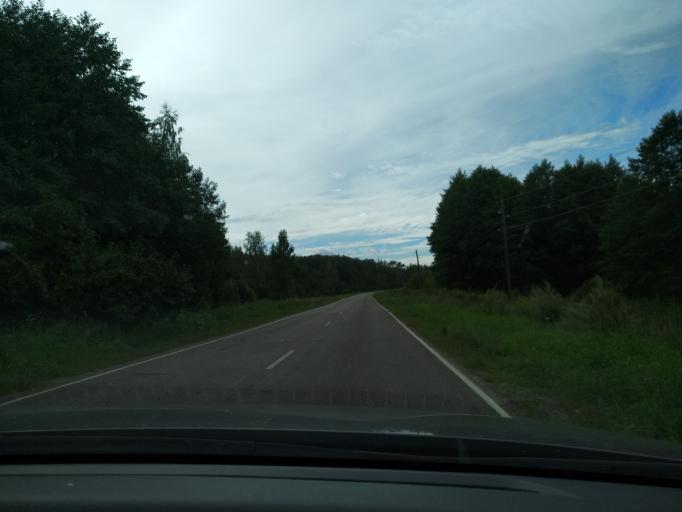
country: RU
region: Moskovskaya
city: Krasnyy Tkach
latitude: 55.3809
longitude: 39.1951
